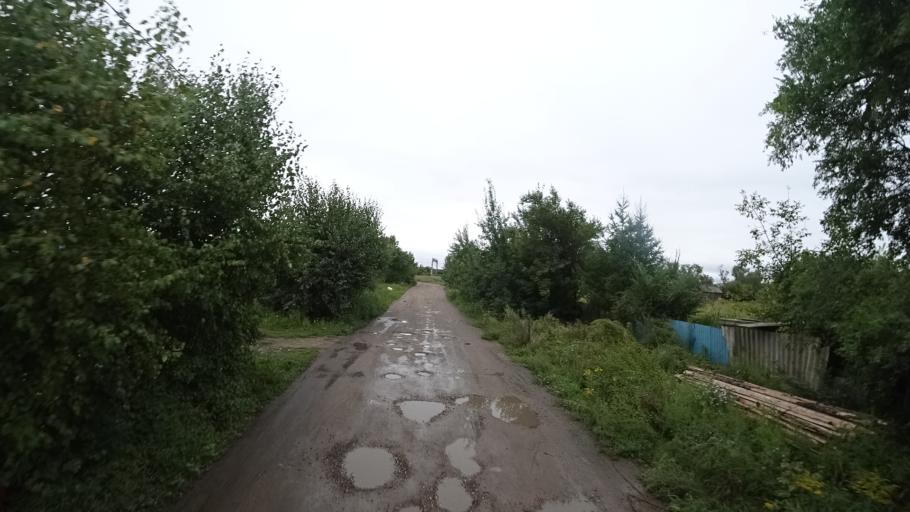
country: RU
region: Primorskiy
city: Chernigovka
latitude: 44.3438
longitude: 132.5340
